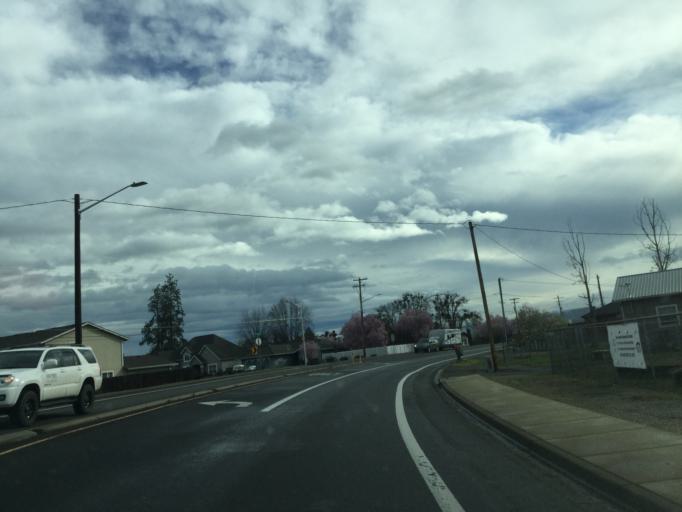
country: US
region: Oregon
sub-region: Jackson County
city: Central Point
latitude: 42.3889
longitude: -122.8904
